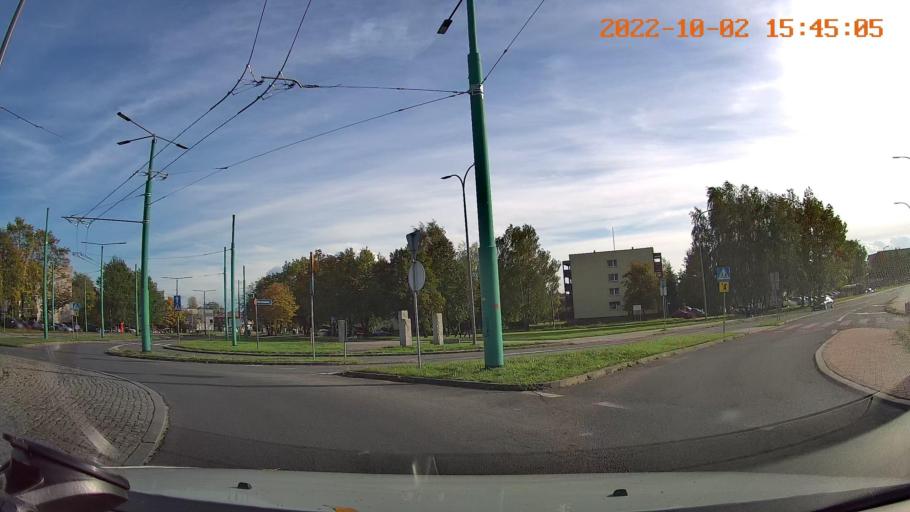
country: PL
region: Silesian Voivodeship
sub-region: Tychy
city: Cielmice
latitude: 50.0984
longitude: 18.9911
